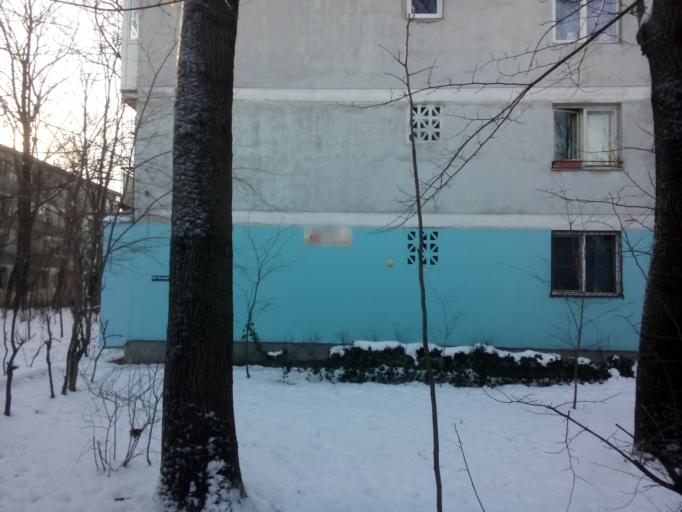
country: RO
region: Bucuresti
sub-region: Municipiul Bucuresti
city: Bucharest
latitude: 44.4289
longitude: 26.1417
